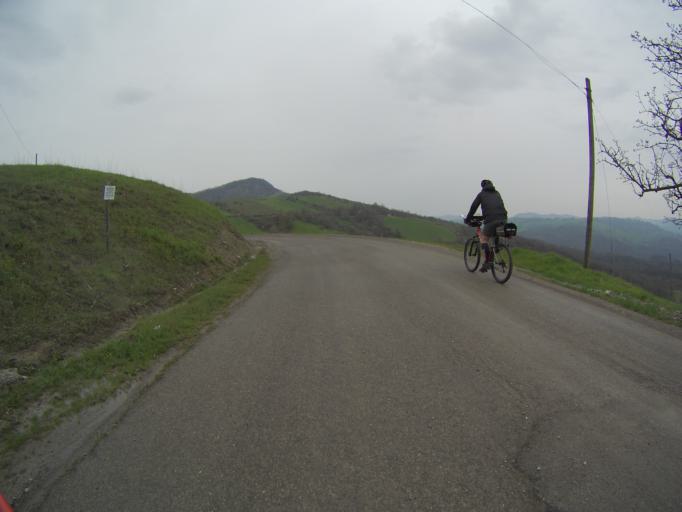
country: IT
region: Emilia-Romagna
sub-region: Provincia di Reggio Emilia
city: Ciano d'Enza
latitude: 44.5424
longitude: 10.4367
